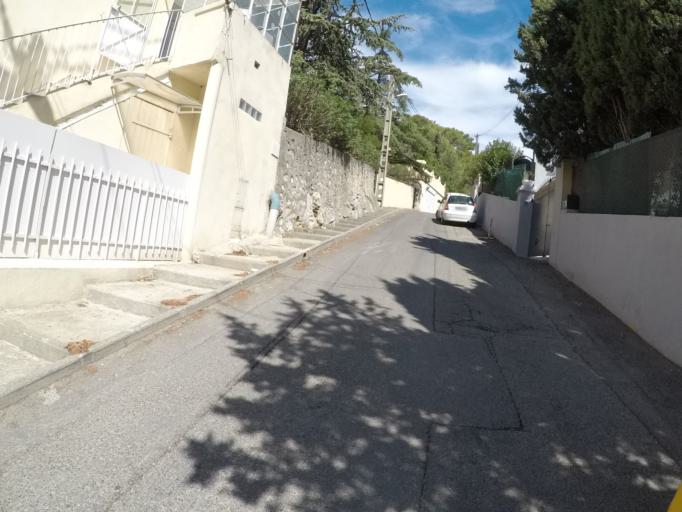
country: FR
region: Provence-Alpes-Cote d'Azur
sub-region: Departement des Bouches-du-Rhone
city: Marseille 09
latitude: 43.2450
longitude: 5.4276
